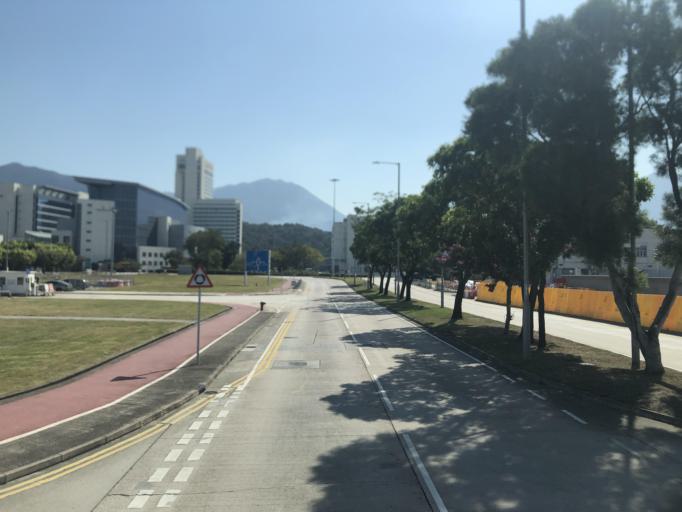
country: HK
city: Tai O
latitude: 22.3006
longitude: 113.9315
